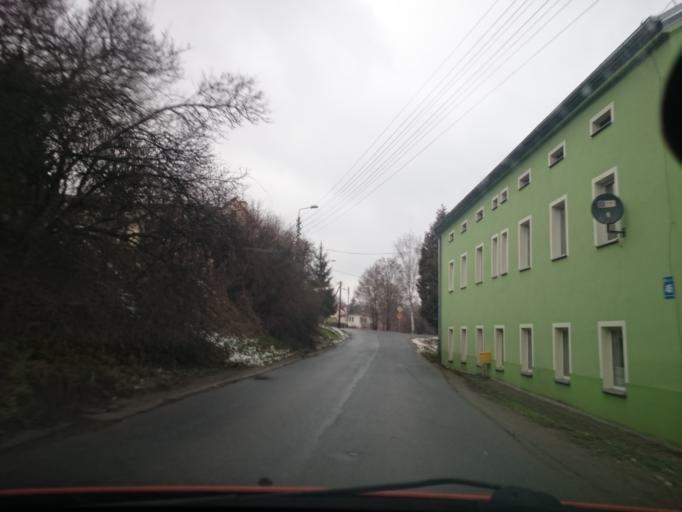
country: PL
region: Lower Silesian Voivodeship
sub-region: Powiat klodzki
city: Klodzko
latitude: 50.4198
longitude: 16.6427
